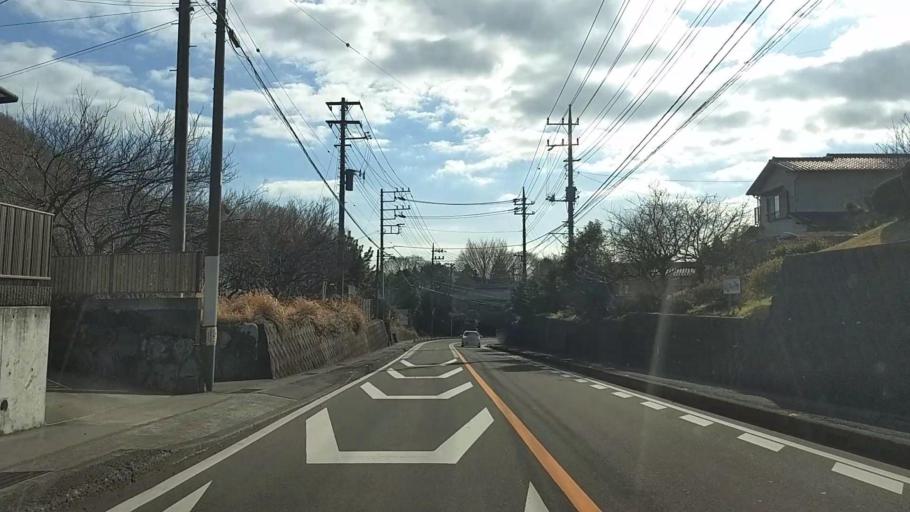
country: JP
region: Kanagawa
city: Isehara
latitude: 35.4409
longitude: 139.3011
